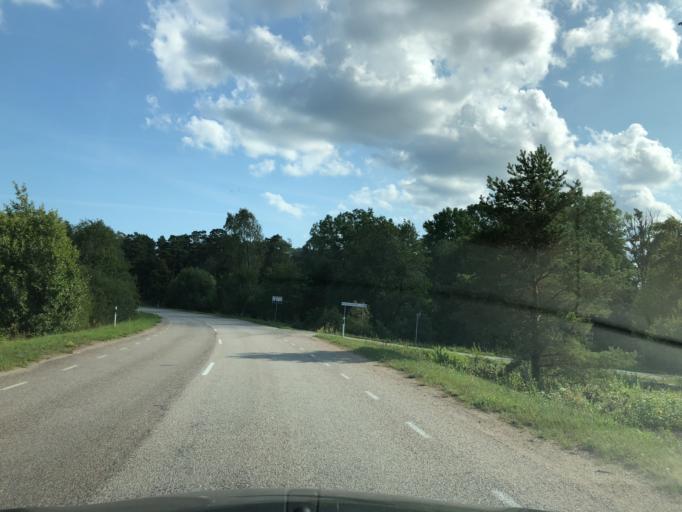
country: EE
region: Hiiumaa
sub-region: Kaerdla linn
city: Kardla
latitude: 58.7089
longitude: 22.5878
